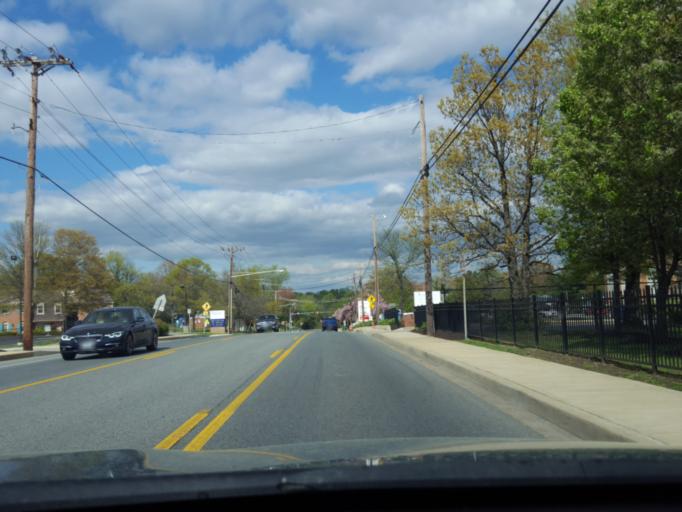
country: US
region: Maryland
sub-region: Charles County
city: La Plata
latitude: 38.5293
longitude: -76.9743
